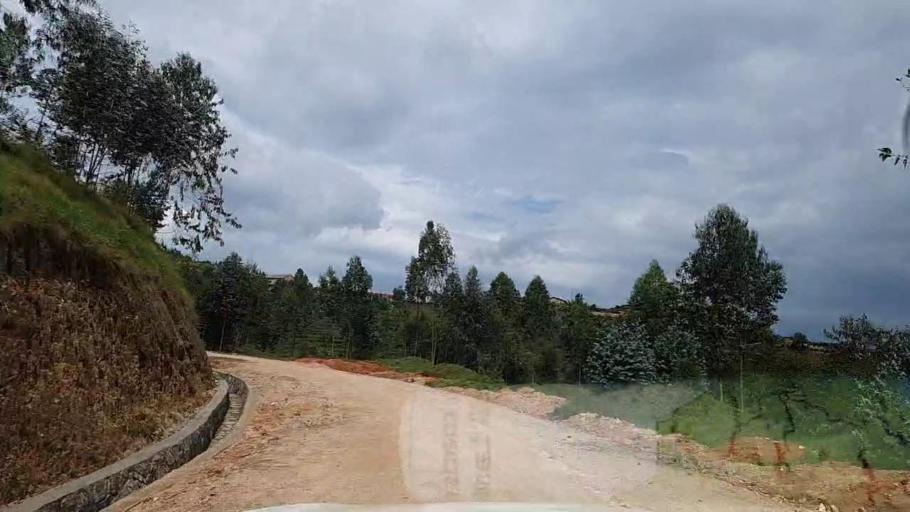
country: RW
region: Southern Province
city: Nzega
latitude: -2.3372
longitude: 29.4409
